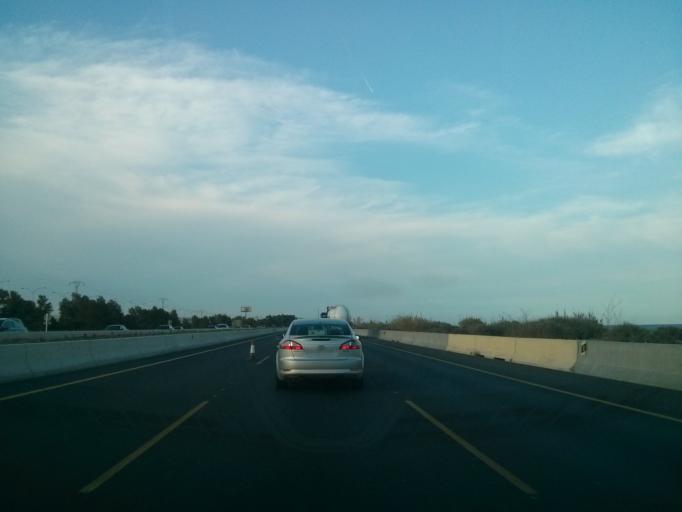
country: ES
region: Valencia
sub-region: Provincia de Valencia
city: Albuixech
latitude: 39.5310
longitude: -0.3114
